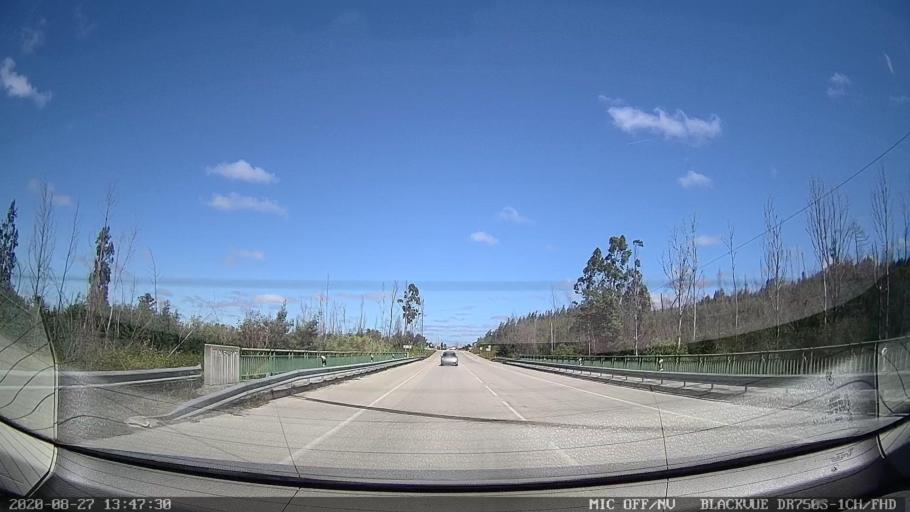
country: PT
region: Coimbra
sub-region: Mira
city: Mira
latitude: 40.3870
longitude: -8.7410
